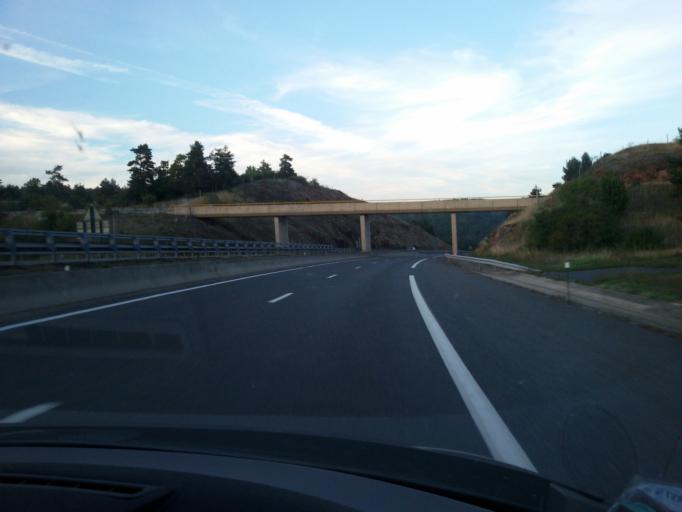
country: FR
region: Midi-Pyrenees
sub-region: Departement de l'Aveyron
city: Severac-le-Chateau
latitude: 44.3556
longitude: 3.1099
